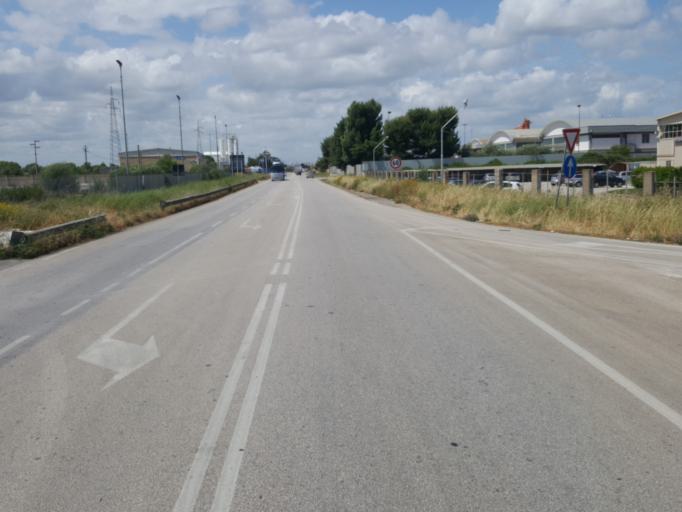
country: IT
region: Apulia
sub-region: Provincia di Bari
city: Modugno
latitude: 41.0933
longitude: 16.7524
